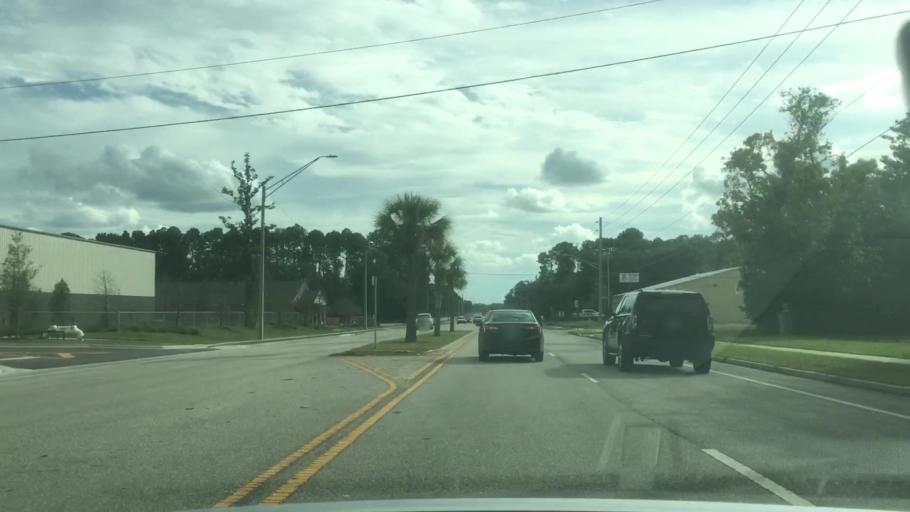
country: US
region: Florida
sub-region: Duval County
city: Atlantic Beach
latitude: 30.3354
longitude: -81.5234
